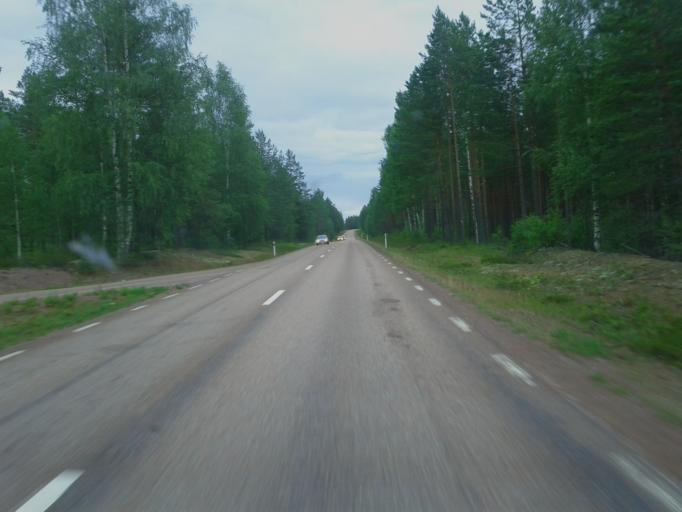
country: SE
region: Dalarna
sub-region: Mora Kommun
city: Mora
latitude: 61.0726
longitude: 14.3651
